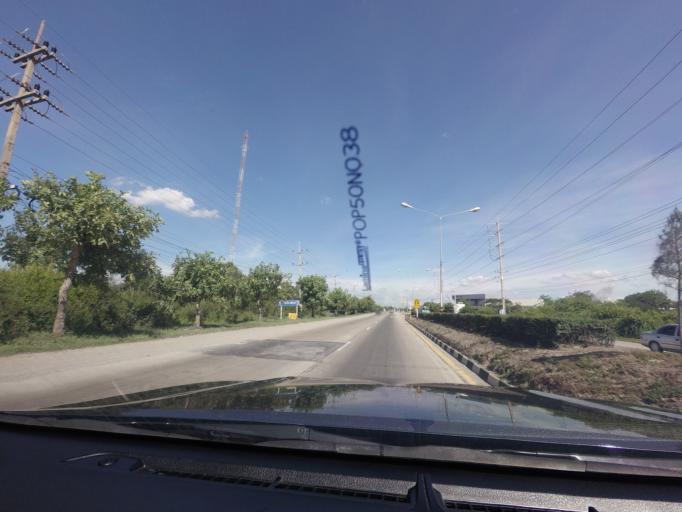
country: TH
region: Suphan Buri
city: Song Phi Nong
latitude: 14.1621
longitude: 99.9769
